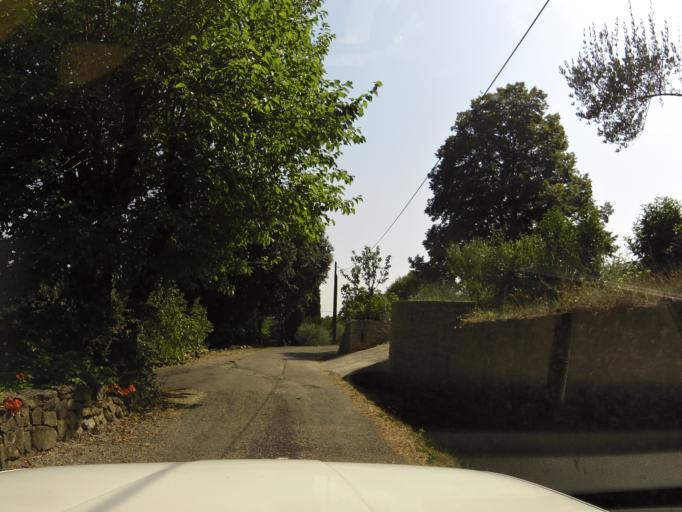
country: FR
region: Languedoc-Roussillon
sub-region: Departement du Gard
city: Anduze
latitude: 44.0959
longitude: 3.9896
